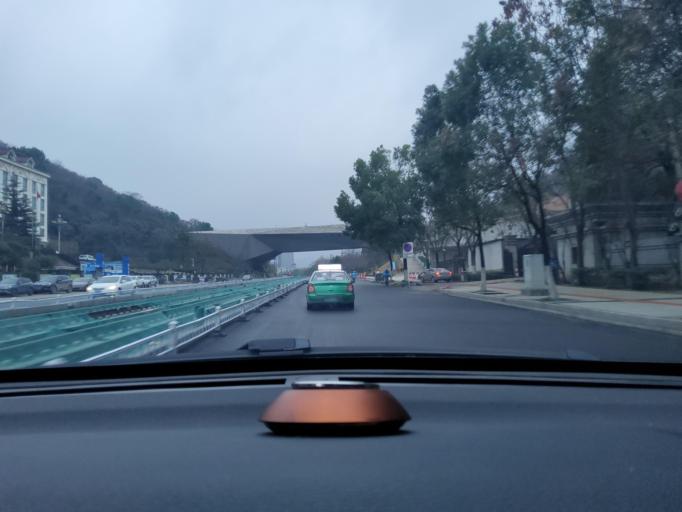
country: CN
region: Hubei
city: Tuanchengshan
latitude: 30.1947
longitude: 115.0213
